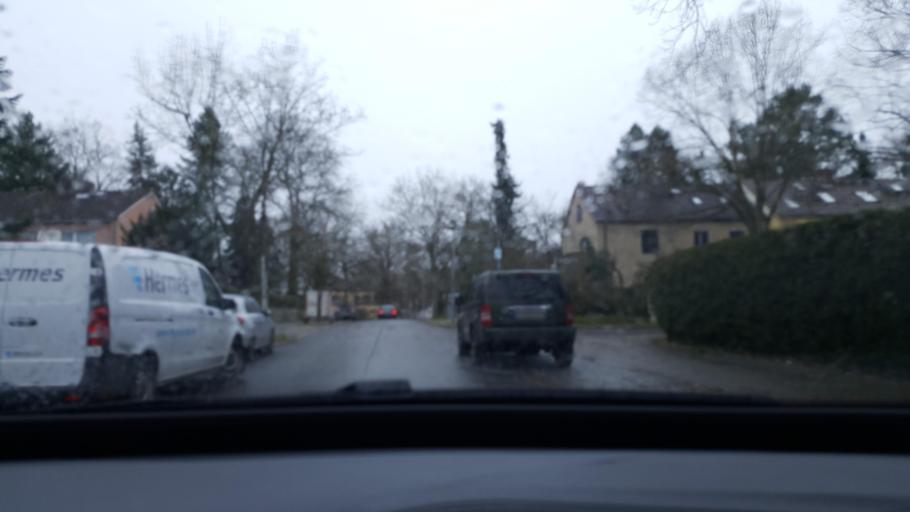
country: DE
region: Berlin
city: Wannsee
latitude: 52.4218
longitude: 13.1615
